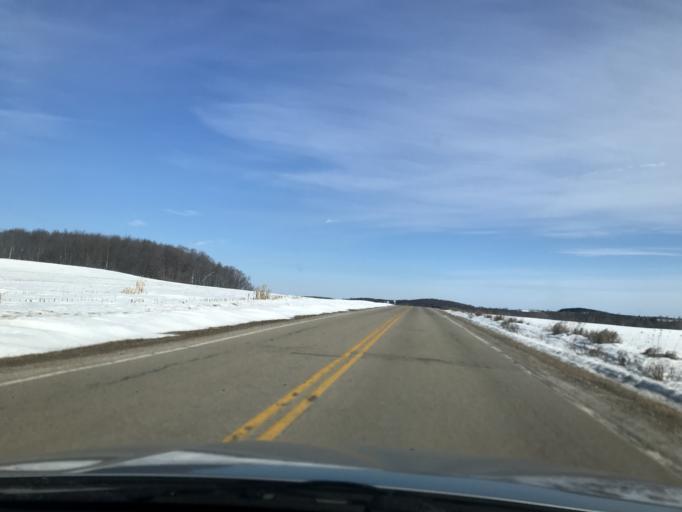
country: US
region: Wisconsin
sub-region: Oconto County
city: Gillett
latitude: 44.9410
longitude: -88.2656
